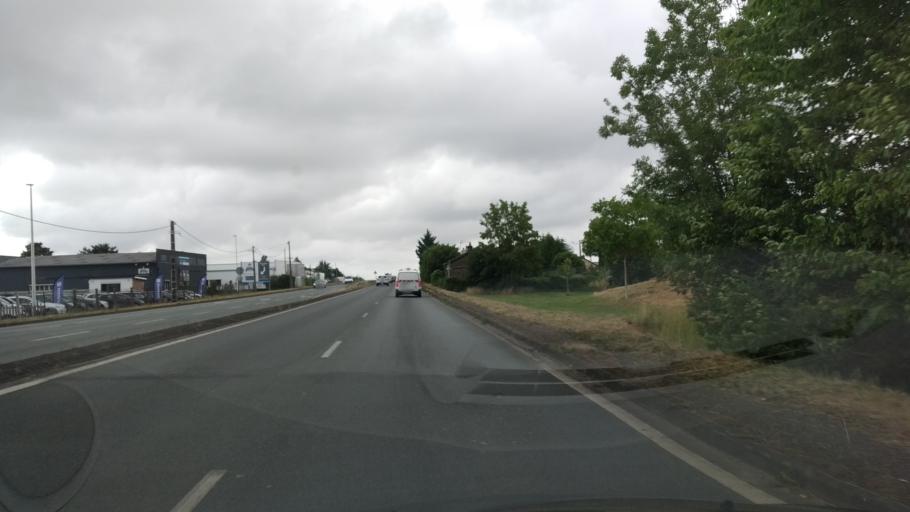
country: FR
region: Poitou-Charentes
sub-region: Departement de la Vienne
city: Biard
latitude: 46.5790
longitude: 0.3151
